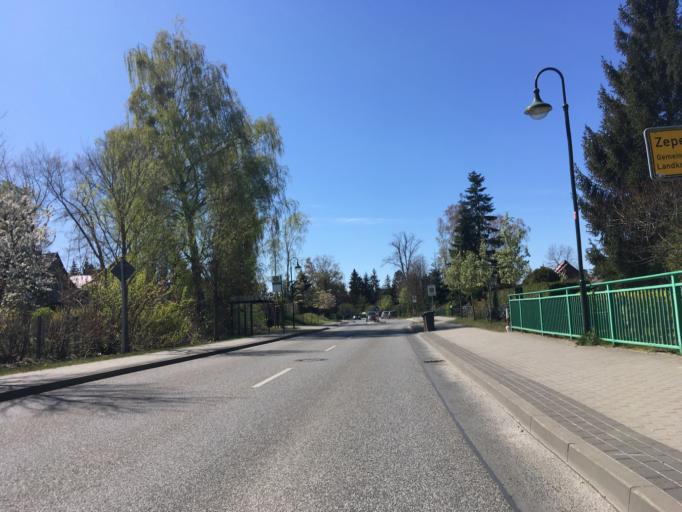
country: DE
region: Brandenburg
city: Bernau bei Berlin
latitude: 52.6608
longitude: 13.5574
